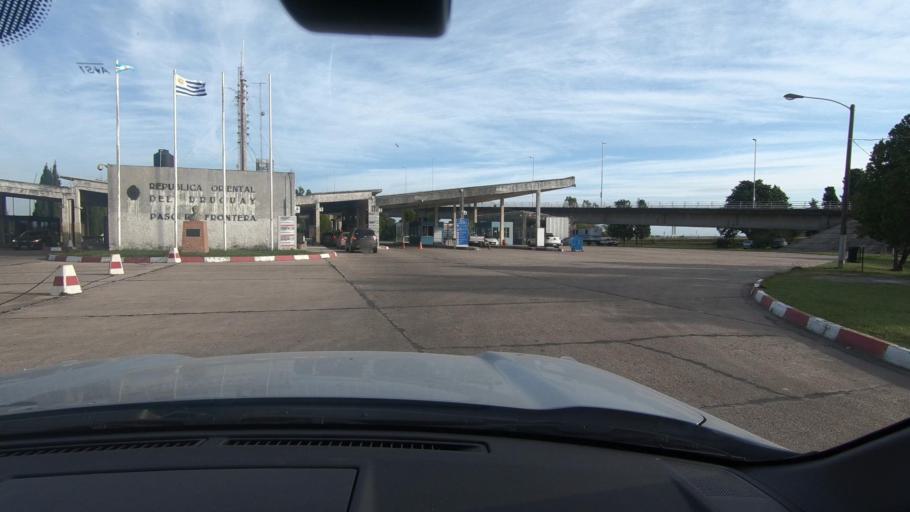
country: AR
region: Entre Rios
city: Colon
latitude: -32.2593
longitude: -58.1346
